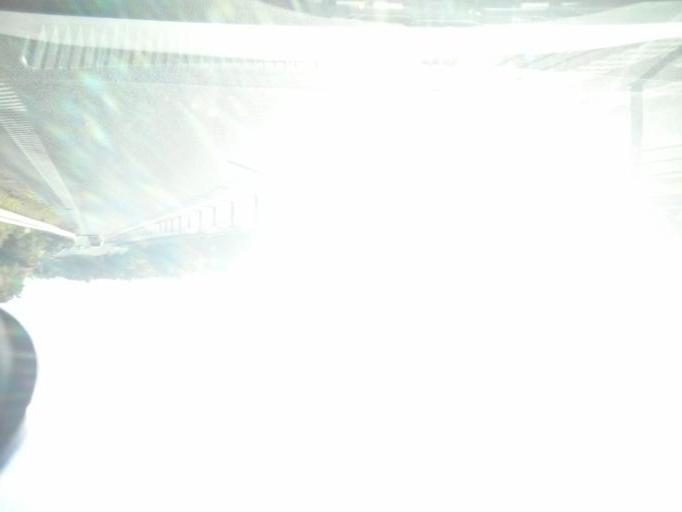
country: SE
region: Blekinge
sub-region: Ronneby Kommun
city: Kallinge
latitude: 56.2299
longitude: 15.2592
